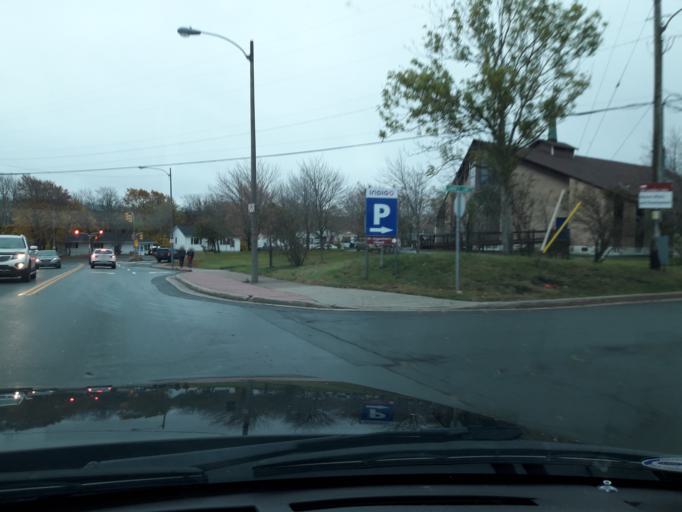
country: CA
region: Newfoundland and Labrador
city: St. John's
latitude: 47.5694
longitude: -52.7349
